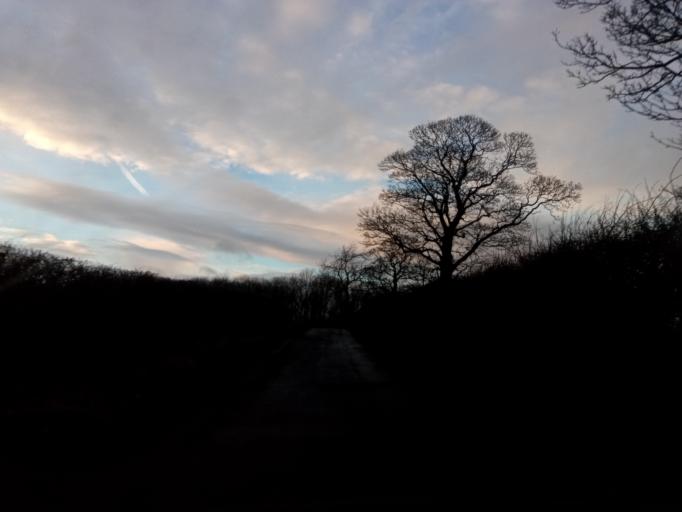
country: GB
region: England
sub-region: Northumberland
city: Ponteland
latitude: 55.0844
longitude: -1.7582
